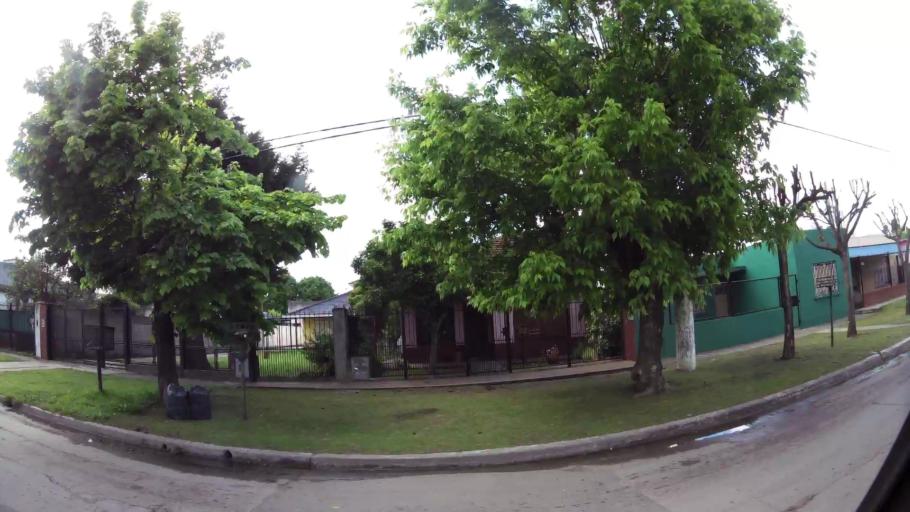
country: AR
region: Buenos Aires
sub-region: Partido de Quilmes
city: Quilmes
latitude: -34.8273
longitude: -58.1867
